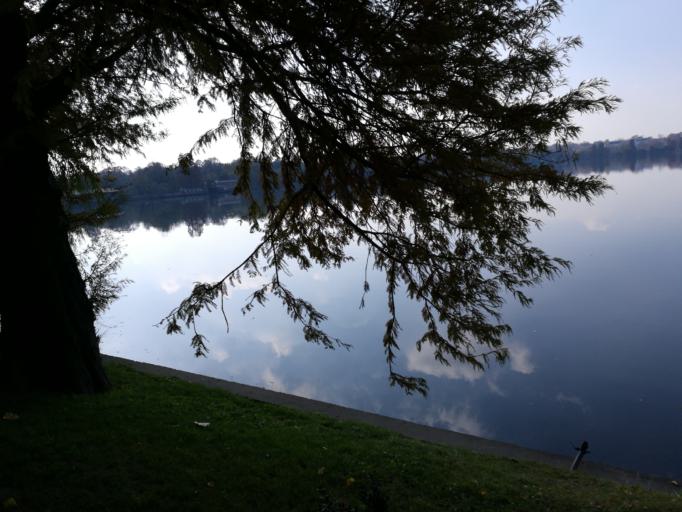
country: RO
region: Bucuresti
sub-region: Municipiul Bucuresti
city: Bucharest
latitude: 44.4761
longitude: 26.0887
